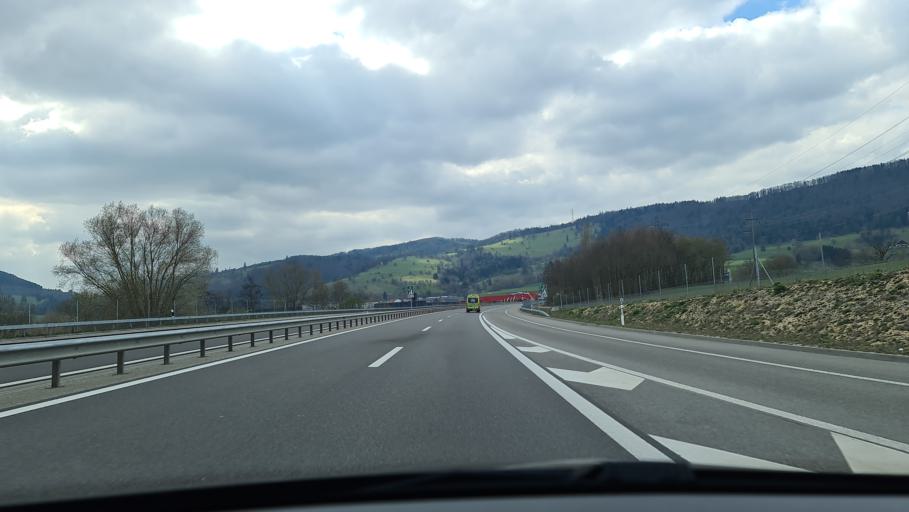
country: CH
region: Jura
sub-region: Delemont District
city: Glovelier
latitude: 47.3410
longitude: 7.2206
